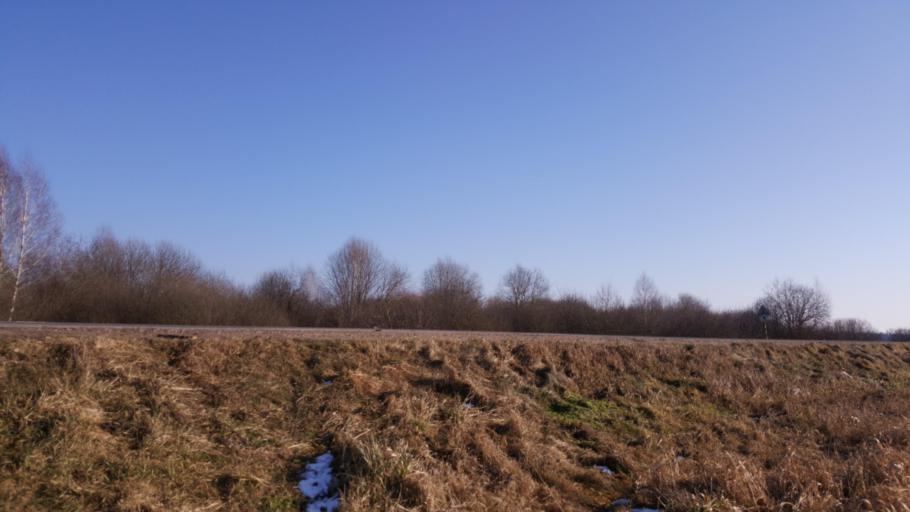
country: BY
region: Brest
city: Kamyanyets
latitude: 52.3860
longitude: 23.7872
